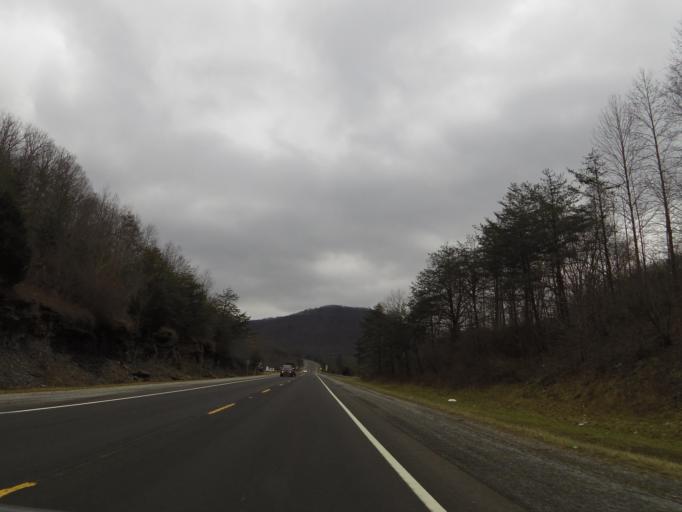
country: US
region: Tennessee
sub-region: Campbell County
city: Caryville
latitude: 36.3933
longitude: -84.3313
